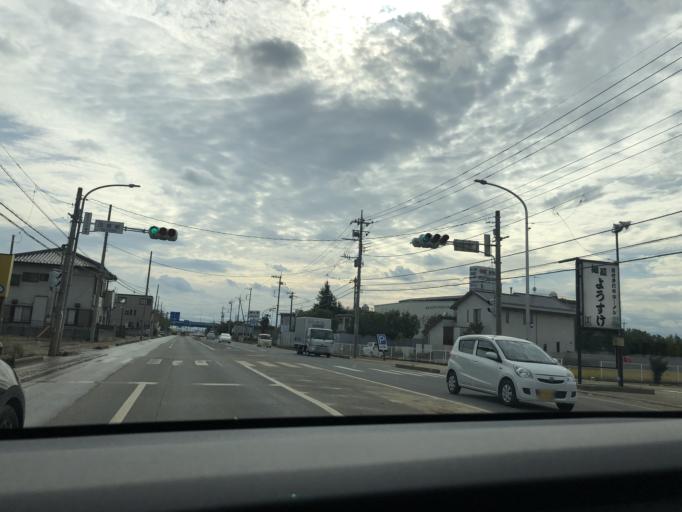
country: JP
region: Tochigi
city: Sano
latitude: 36.2910
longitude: 139.5648
